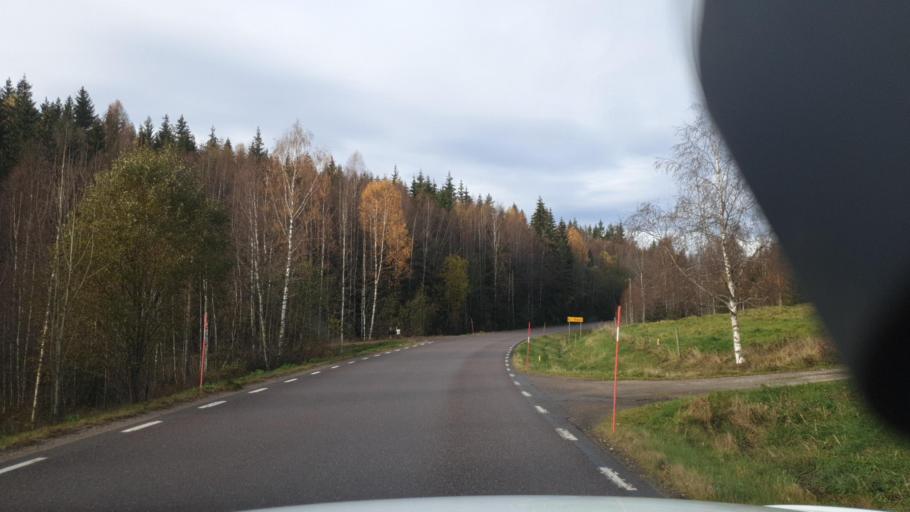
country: SE
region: Vaermland
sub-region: Eda Kommun
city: Charlottenberg
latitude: 59.8744
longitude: 12.3907
